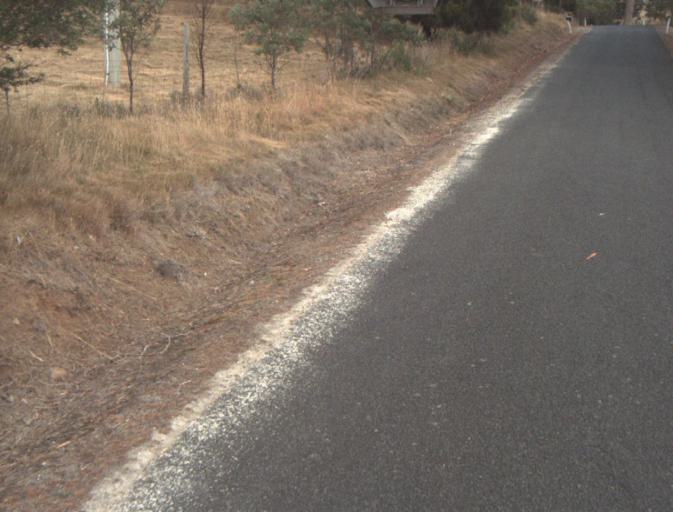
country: AU
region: Tasmania
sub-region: Launceston
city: Mayfield
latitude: -41.2957
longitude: 147.0298
